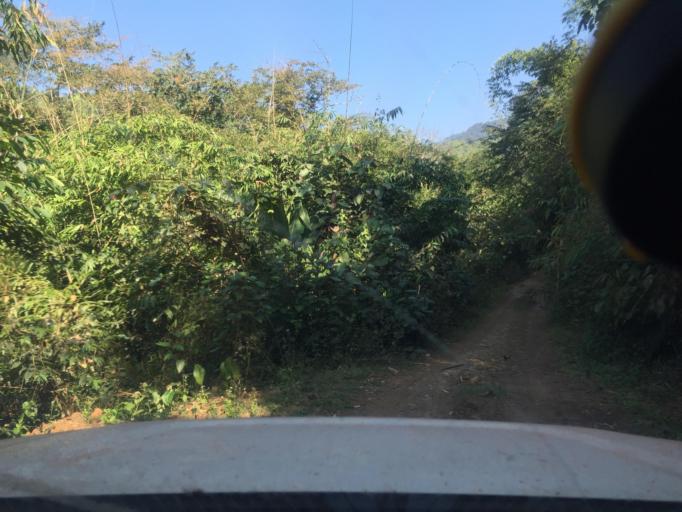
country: LA
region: Phongsali
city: Phongsali
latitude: 21.7023
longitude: 102.3938
